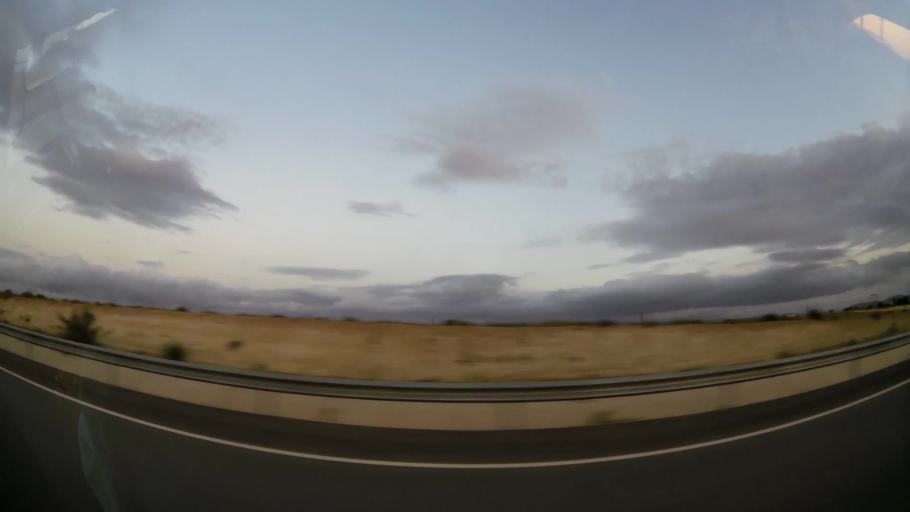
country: MA
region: Oriental
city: El Aioun
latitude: 34.6241
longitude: -2.5398
